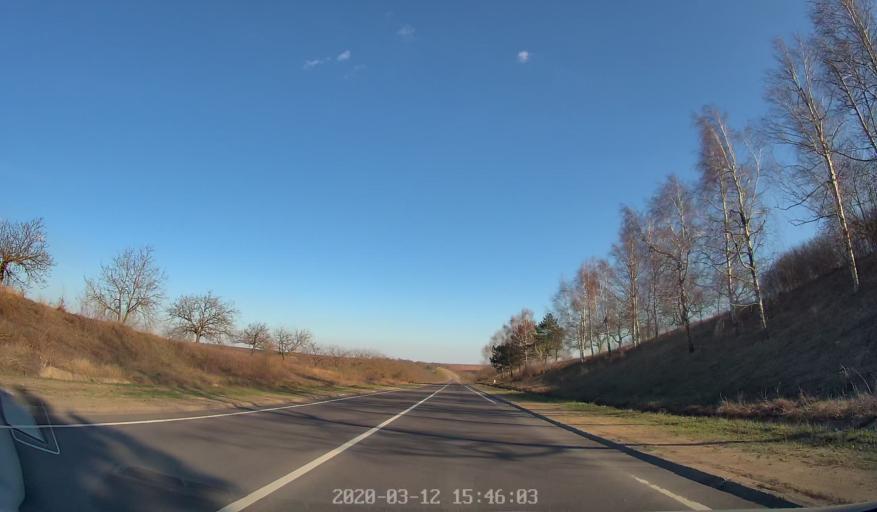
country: MD
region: Chisinau
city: Stauceni
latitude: 47.1020
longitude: 28.8857
